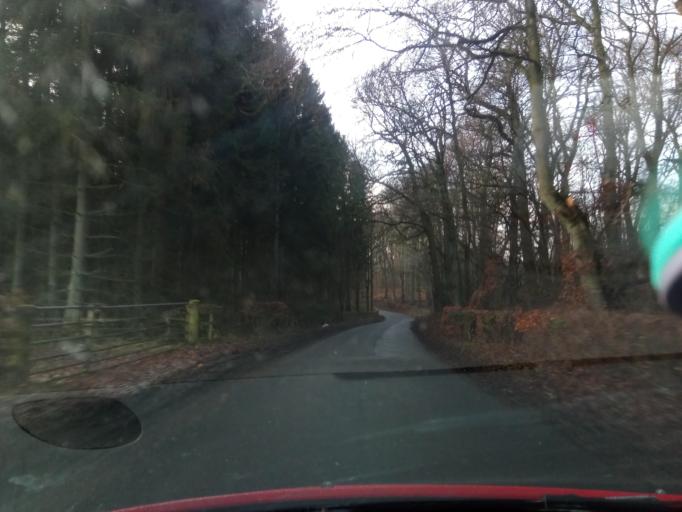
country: GB
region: Scotland
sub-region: The Scottish Borders
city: Hawick
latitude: 55.4400
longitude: -2.7559
